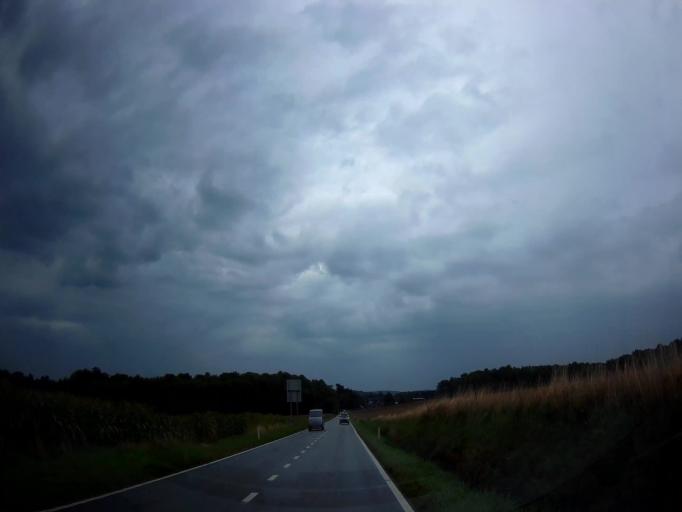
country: BE
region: Wallonia
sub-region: Province de Liege
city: Ferrieres
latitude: 50.4485
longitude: 5.6249
